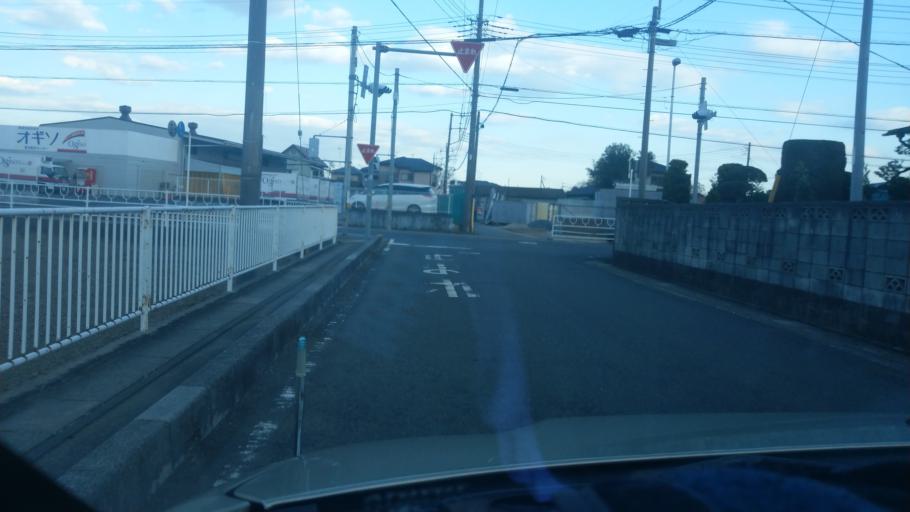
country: JP
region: Saitama
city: Yono
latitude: 35.8925
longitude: 139.5893
